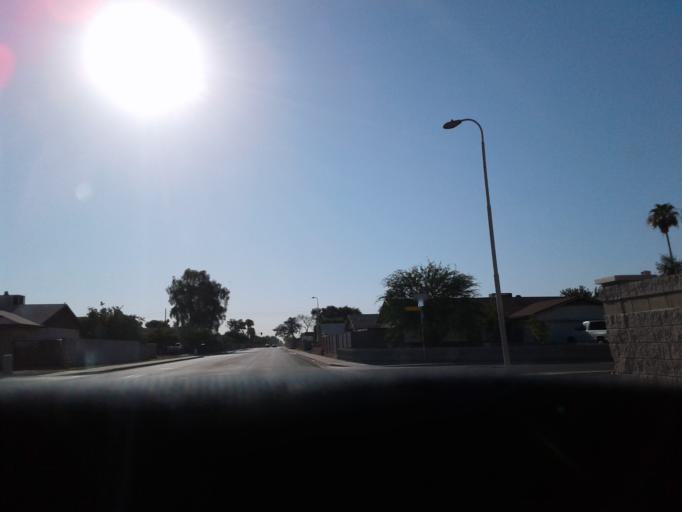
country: US
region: Arizona
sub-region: Maricopa County
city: Tolleson
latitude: 33.4588
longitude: -112.1897
